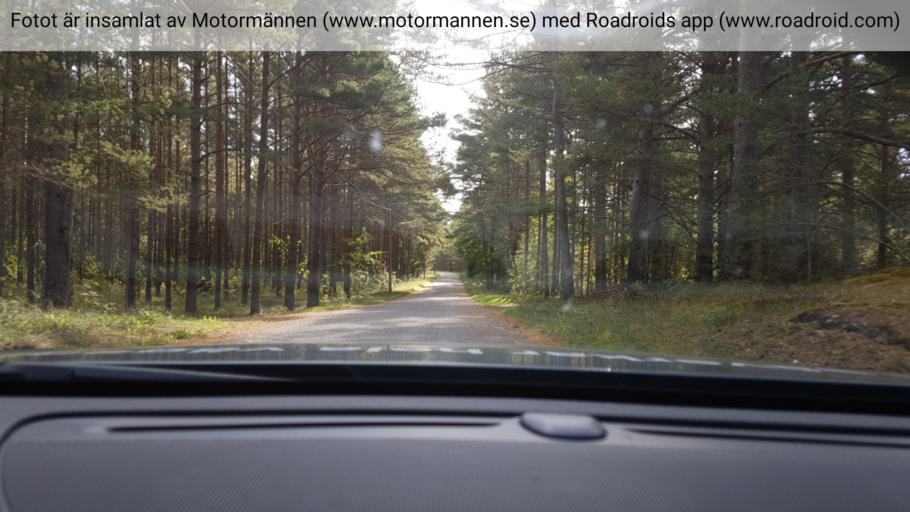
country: SE
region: Gotland
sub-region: Gotland
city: Slite
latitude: 57.9616
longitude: 19.3348
